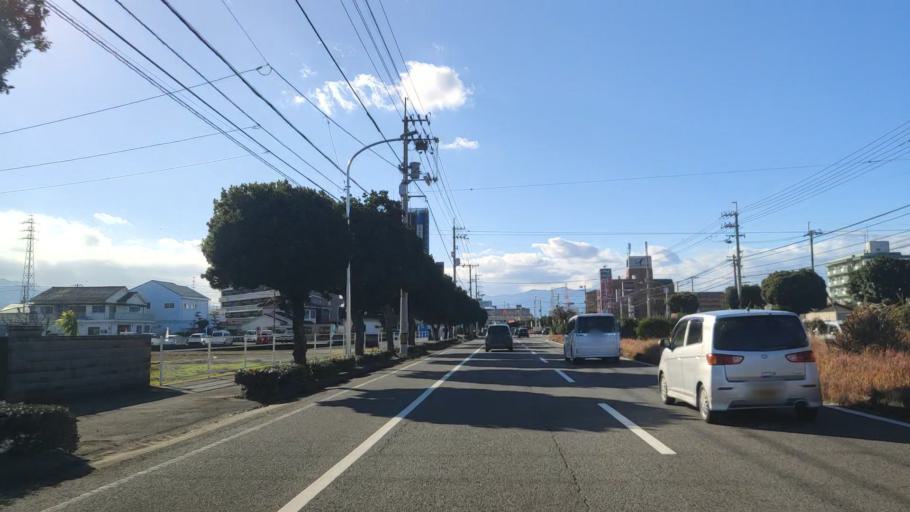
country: JP
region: Ehime
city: Saijo
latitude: 33.9278
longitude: 133.1821
